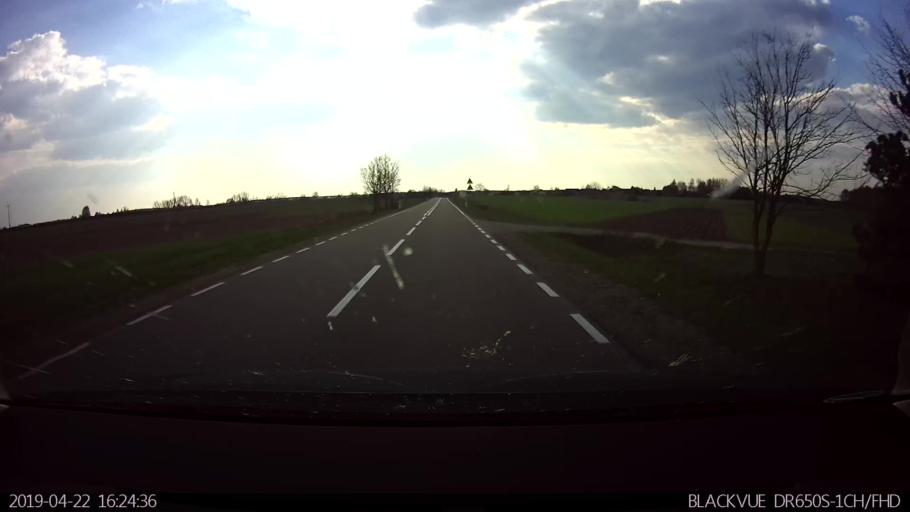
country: PL
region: Podlasie
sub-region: Powiat hajnowski
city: Kleszczele
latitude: 52.5545
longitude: 23.2602
